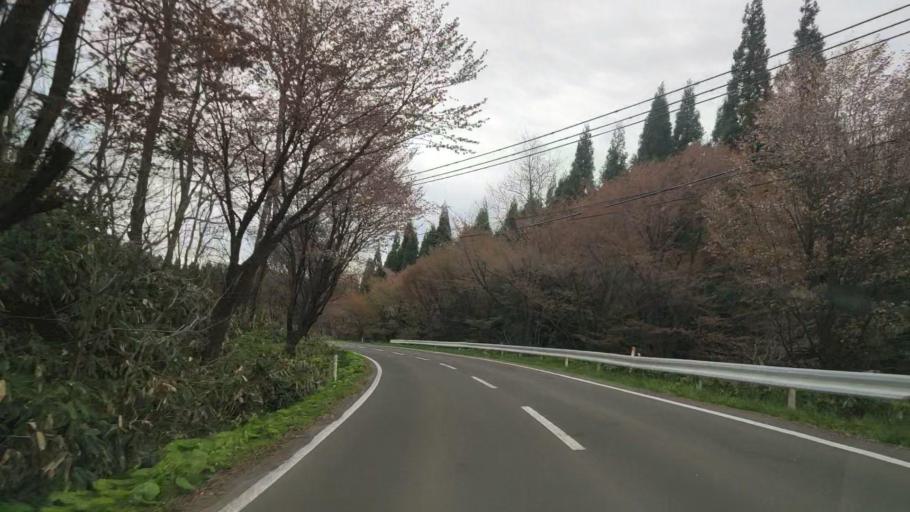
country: JP
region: Akita
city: Hanawa
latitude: 40.3497
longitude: 140.7751
